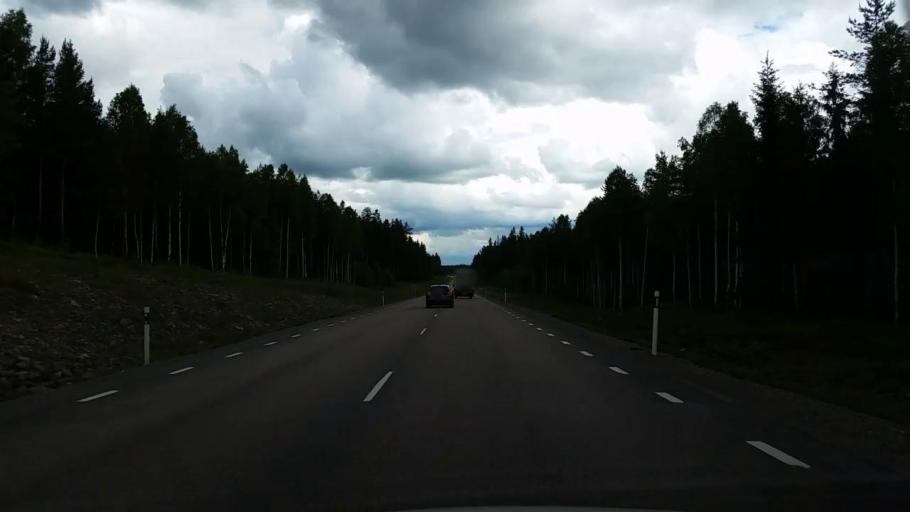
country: SE
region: Dalarna
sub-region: Avesta Kommun
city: Horndal
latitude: 60.4560
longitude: 16.4452
